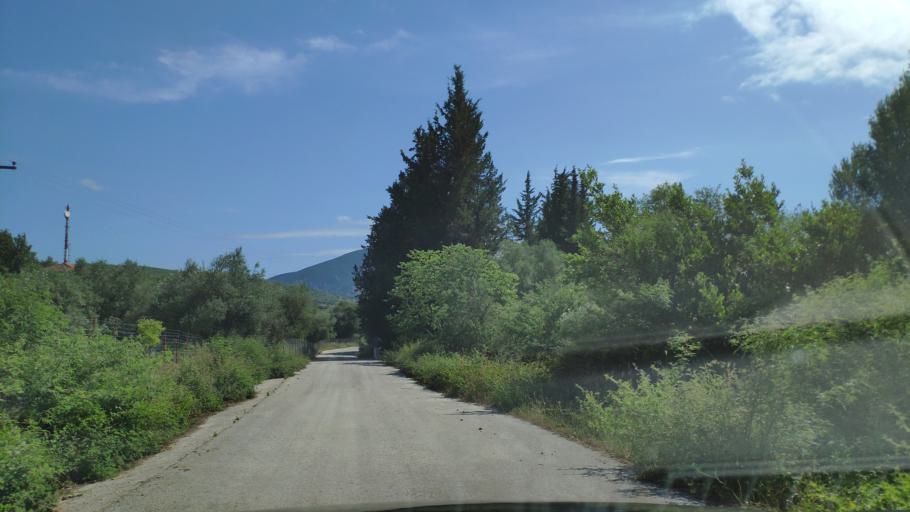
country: AL
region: Vlore
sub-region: Rrethi i Sarandes
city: Konispol
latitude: 39.6219
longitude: 20.2009
